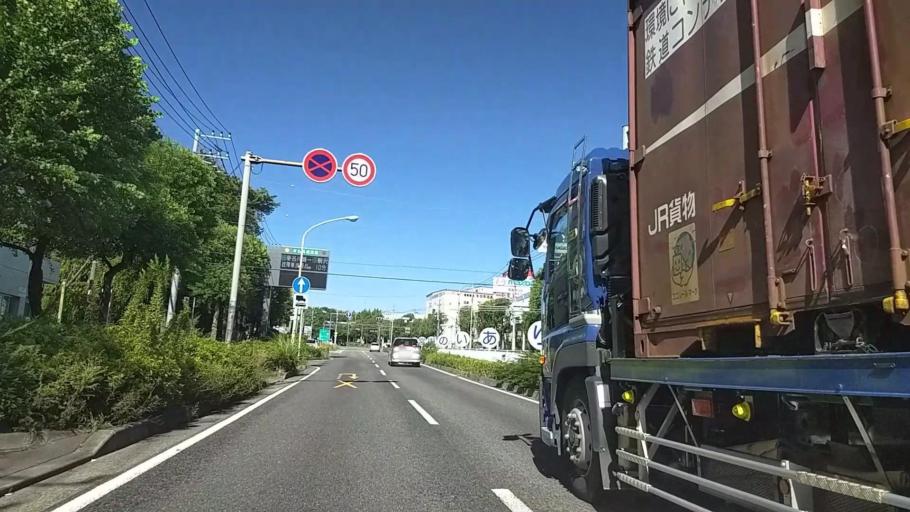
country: JP
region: Tokyo
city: Chofugaoka
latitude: 35.5875
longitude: 139.5721
